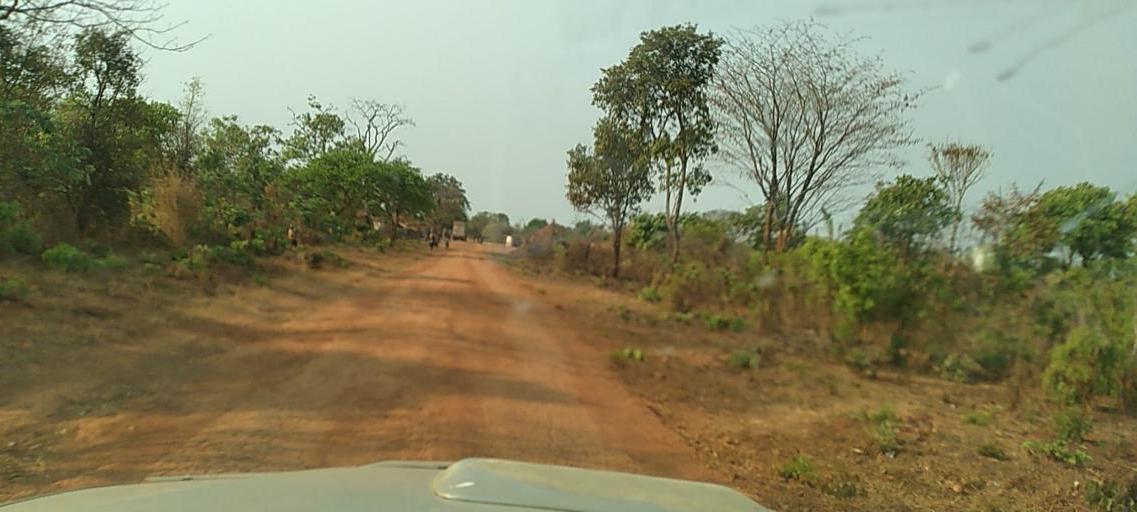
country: ZM
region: North-Western
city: Kasempa
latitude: -13.3041
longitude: 26.5535
